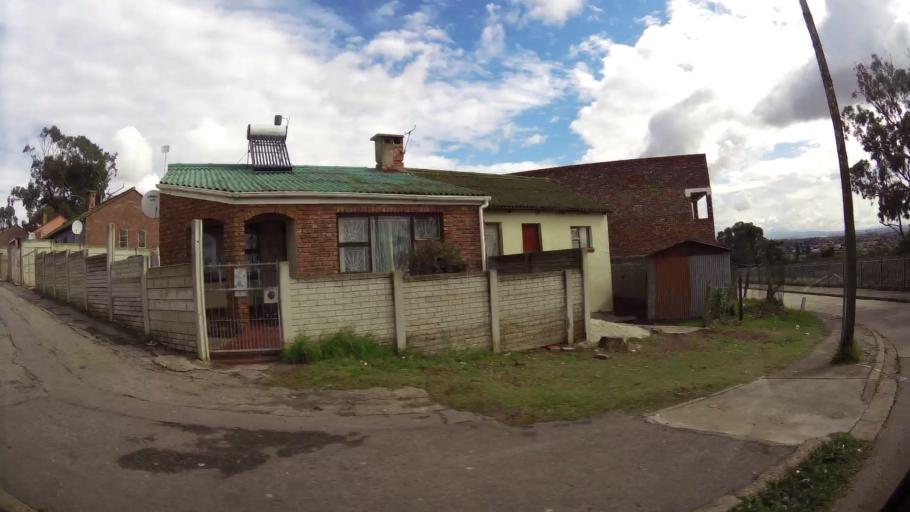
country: ZA
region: Eastern Cape
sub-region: Nelson Mandela Bay Metropolitan Municipality
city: Port Elizabeth
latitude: -33.9309
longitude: 25.5675
